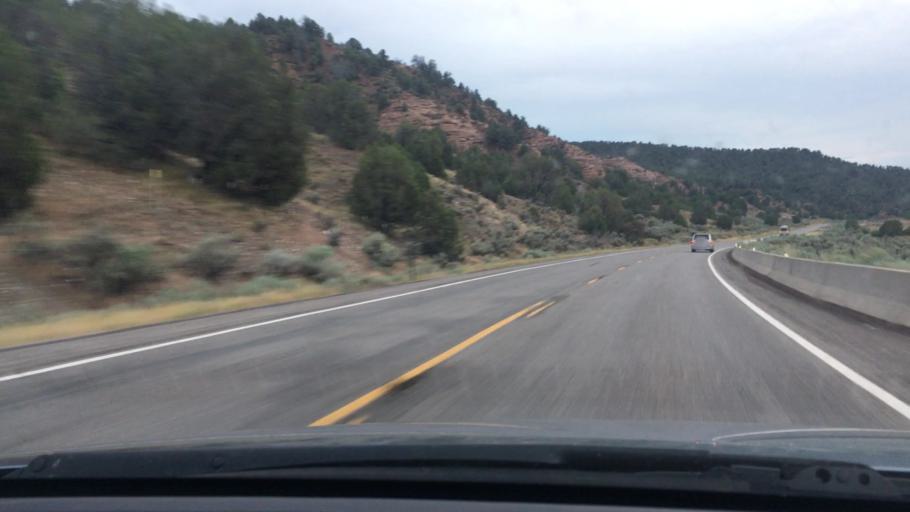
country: US
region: Utah
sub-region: Utah County
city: Woodland Hills
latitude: 39.9302
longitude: -111.5435
